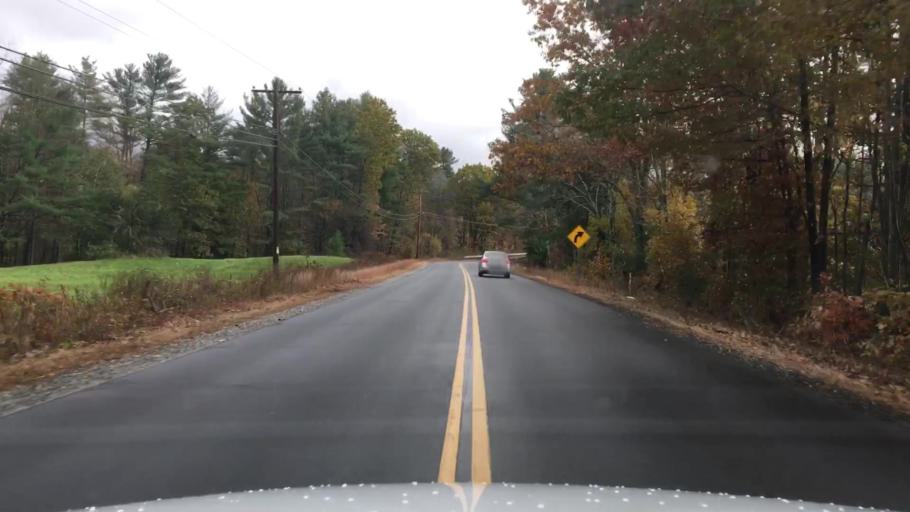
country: US
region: New Hampshire
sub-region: Strafford County
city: Lee
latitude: 43.1092
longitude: -70.9966
